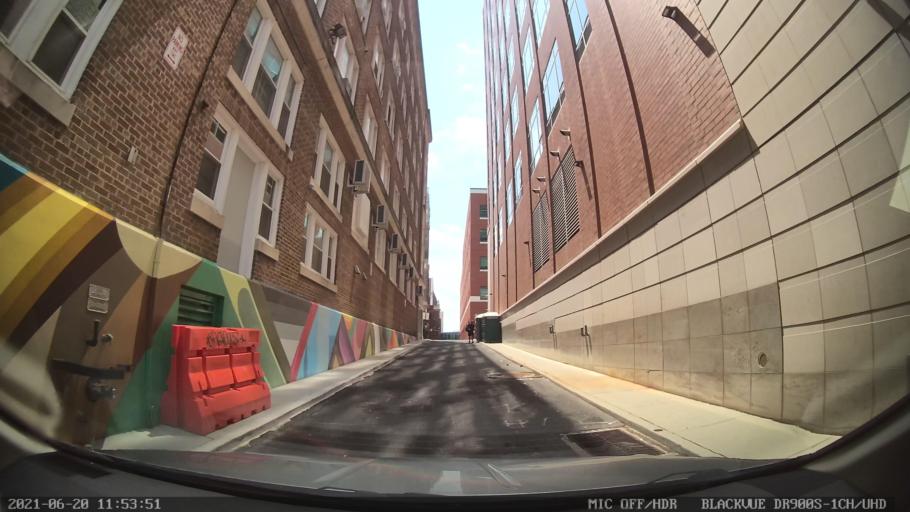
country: US
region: Pennsylvania
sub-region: Lehigh County
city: Allentown
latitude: 40.6033
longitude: -75.4709
